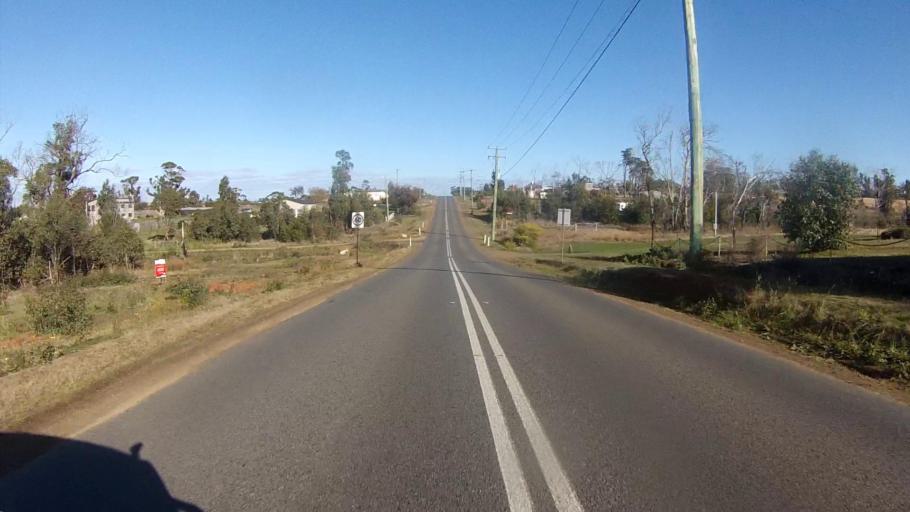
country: AU
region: Tasmania
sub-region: Sorell
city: Sorell
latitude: -42.8802
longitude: 147.8197
